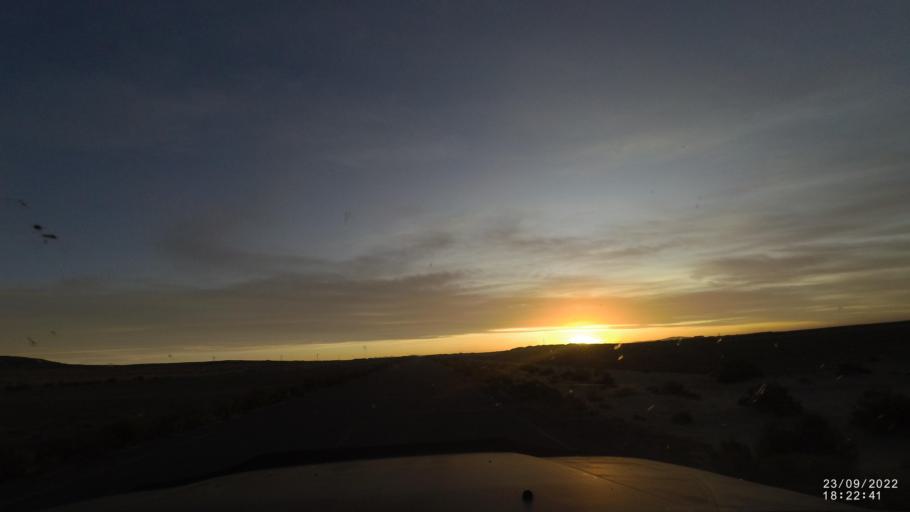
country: BO
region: Oruro
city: Challapata
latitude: -19.2900
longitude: -67.0903
